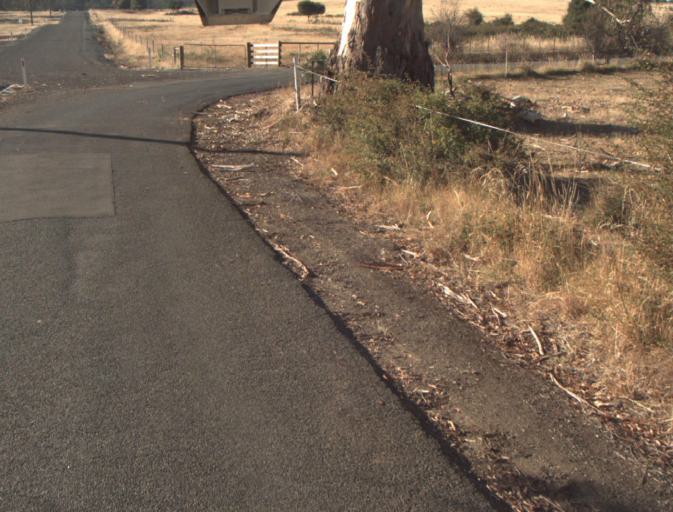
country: AU
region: Tasmania
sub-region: Launceston
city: Newstead
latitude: -41.4337
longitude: 147.2139
